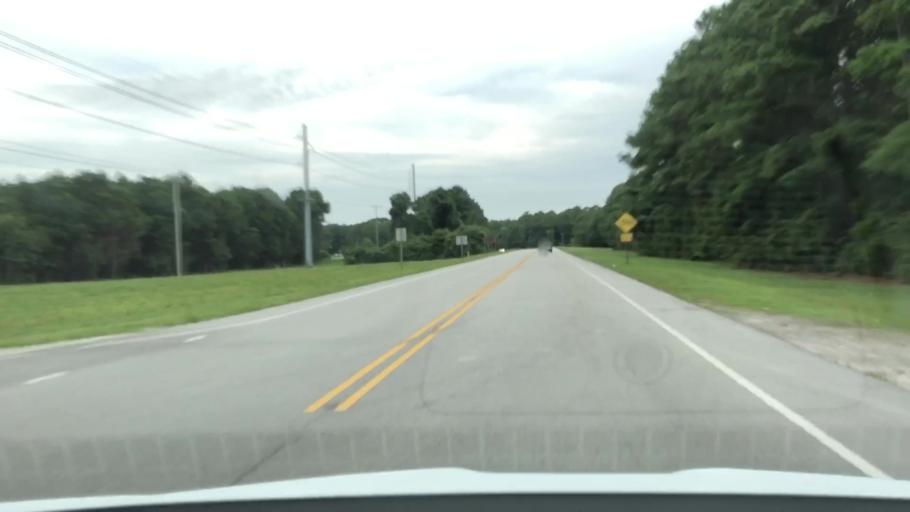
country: US
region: North Carolina
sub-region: Carteret County
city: Cape Carteret
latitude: 34.6985
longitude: -77.0688
